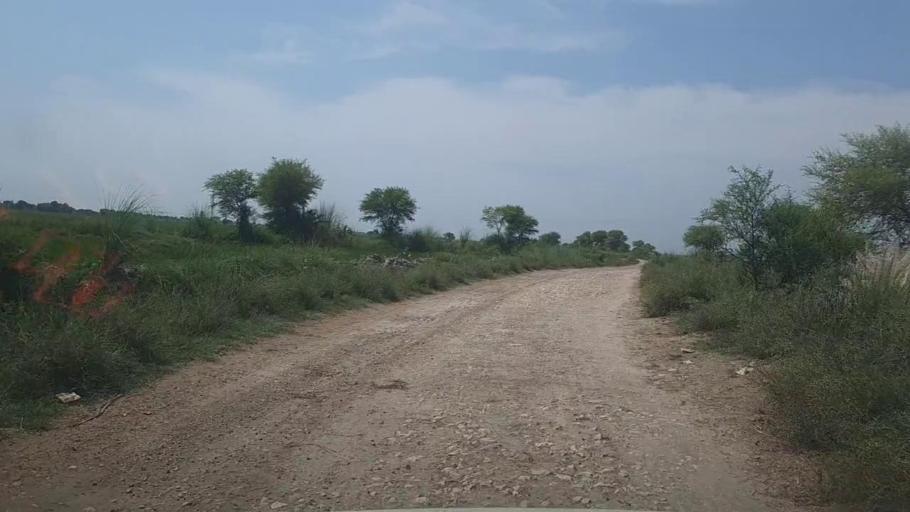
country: PK
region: Sindh
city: Kandhkot
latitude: 28.3091
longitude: 69.2408
